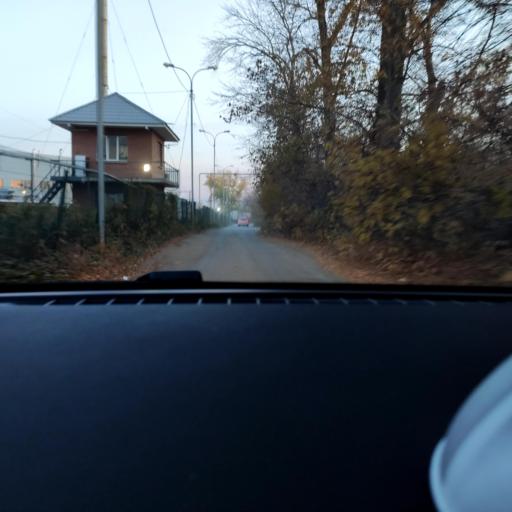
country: RU
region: Samara
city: Petra-Dubrava
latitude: 53.3212
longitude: 50.2944
